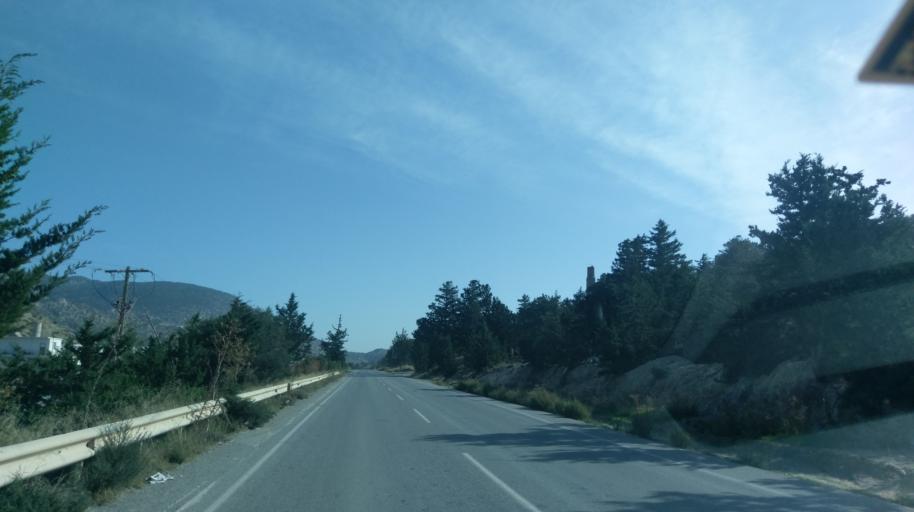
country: CY
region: Lefkosia
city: Nicosia
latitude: 35.2686
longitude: 33.4712
